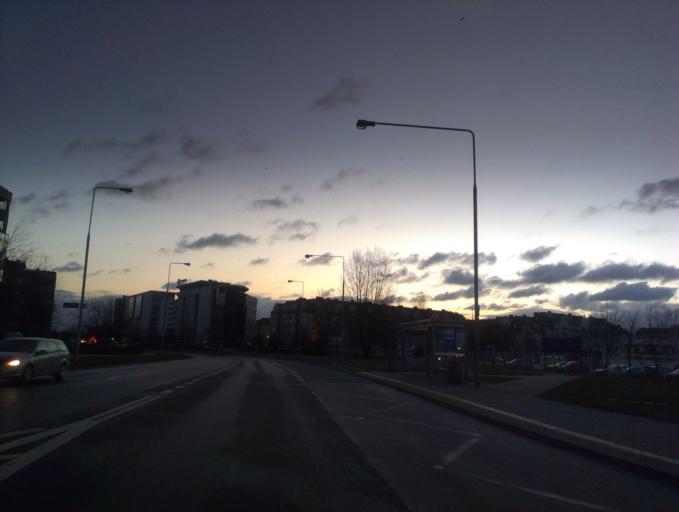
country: PL
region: Masovian Voivodeship
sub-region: Warszawa
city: Kabaty
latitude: 52.1312
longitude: 21.0671
